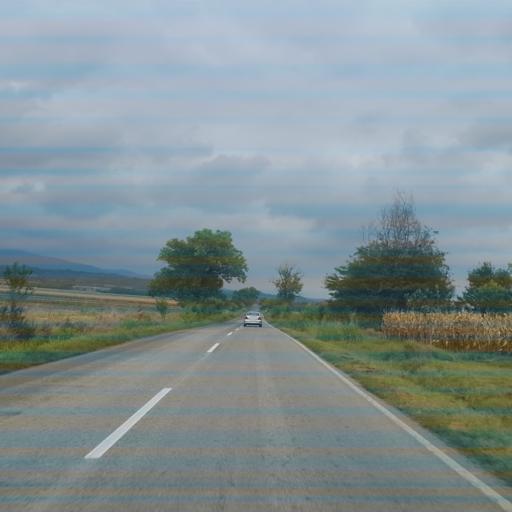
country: RS
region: Central Serbia
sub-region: Nisavski Okrug
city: Aleksinac
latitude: 43.5933
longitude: 21.6338
